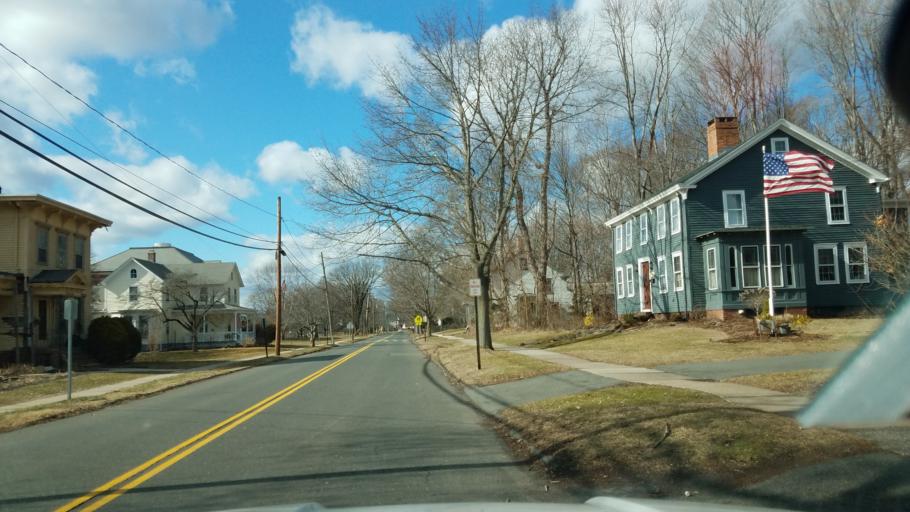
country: US
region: Connecticut
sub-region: Hartford County
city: Wethersfield
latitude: 41.7159
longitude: -72.6567
